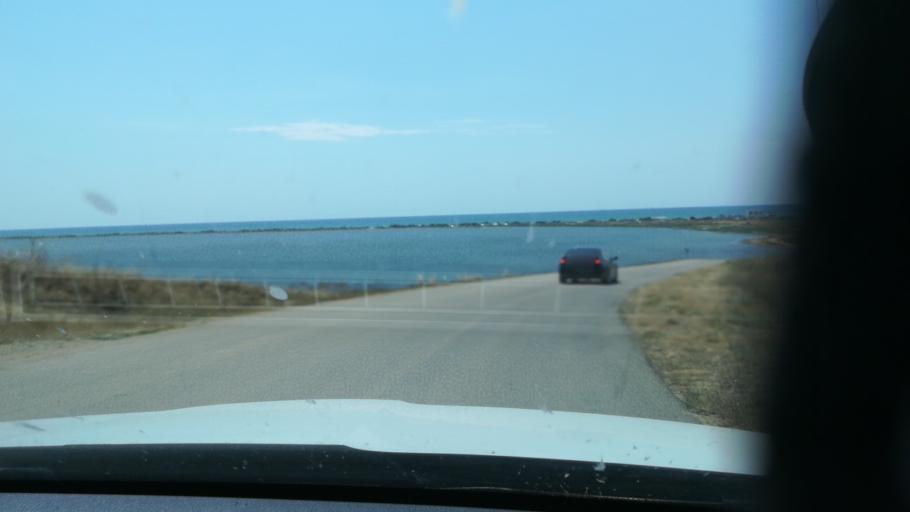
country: RU
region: Krasnodarskiy
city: Vyshestebliyevskaya
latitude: 45.1180
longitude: 36.8952
